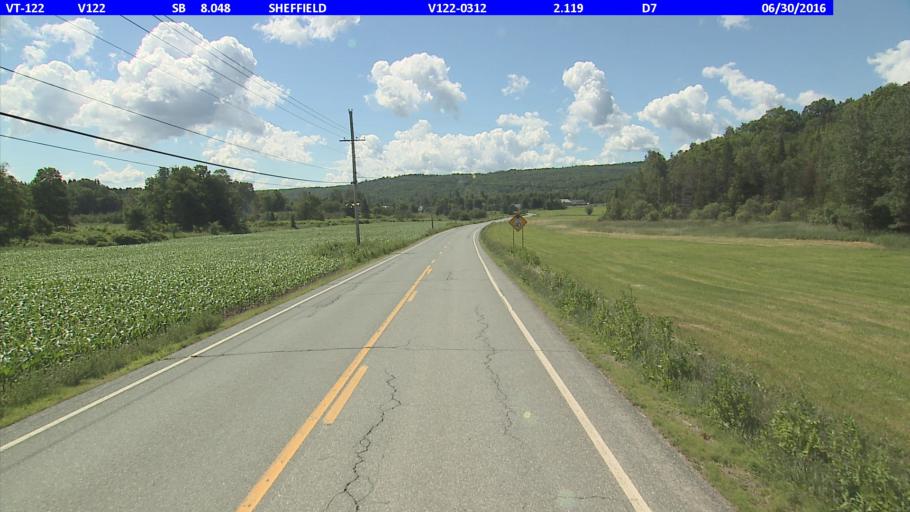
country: US
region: Vermont
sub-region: Caledonia County
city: Lyndonville
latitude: 44.6103
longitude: -72.1213
